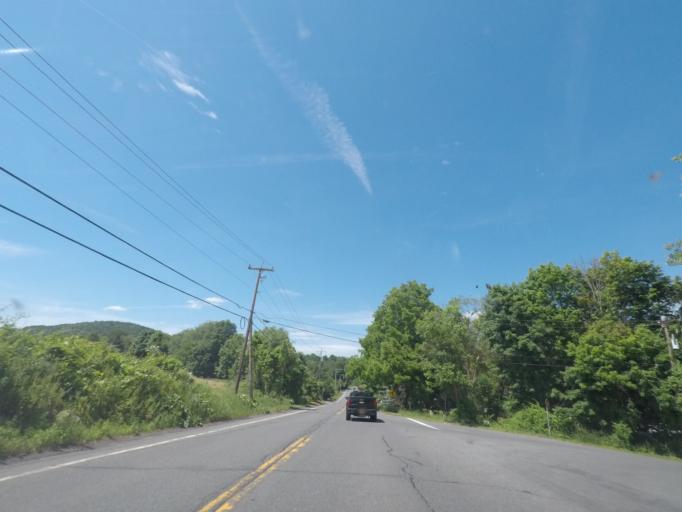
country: US
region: Massachusetts
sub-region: Berkshire County
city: Housatonic
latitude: 42.2162
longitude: -73.5065
